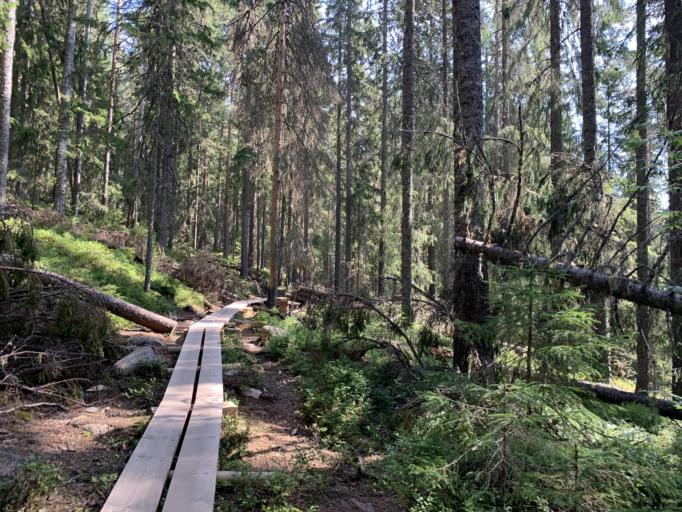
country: SE
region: Vaesternorrland
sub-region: OErnskoeldsviks Kommun
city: Kopmanholmen
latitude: 63.0879
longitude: 18.4889
